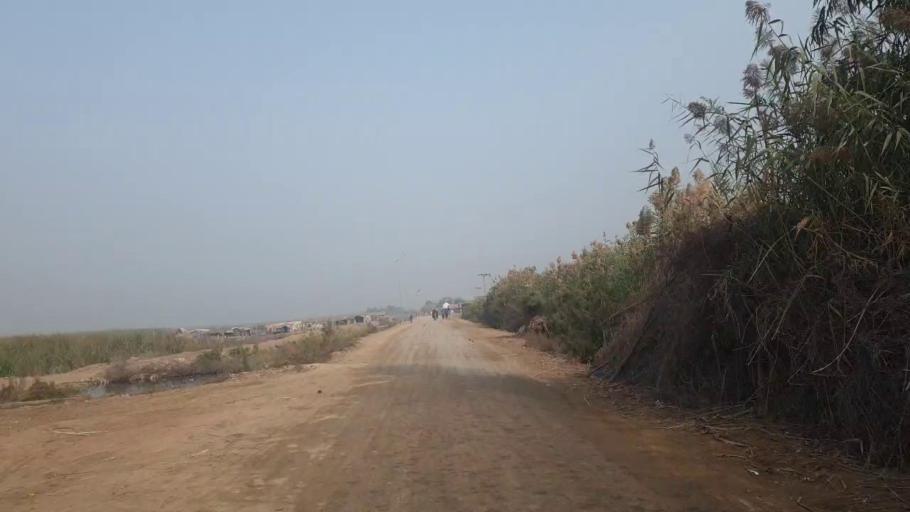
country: PK
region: Sindh
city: Tando Adam
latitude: 25.7984
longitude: 68.6103
